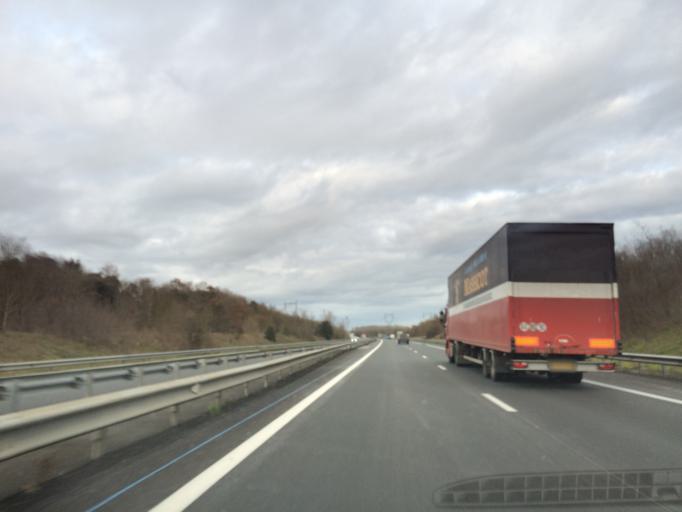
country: FR
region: Poitou-Charentes
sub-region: Departement des Deux-Sevres
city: Fors
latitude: 46.2435
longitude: -0.4309
